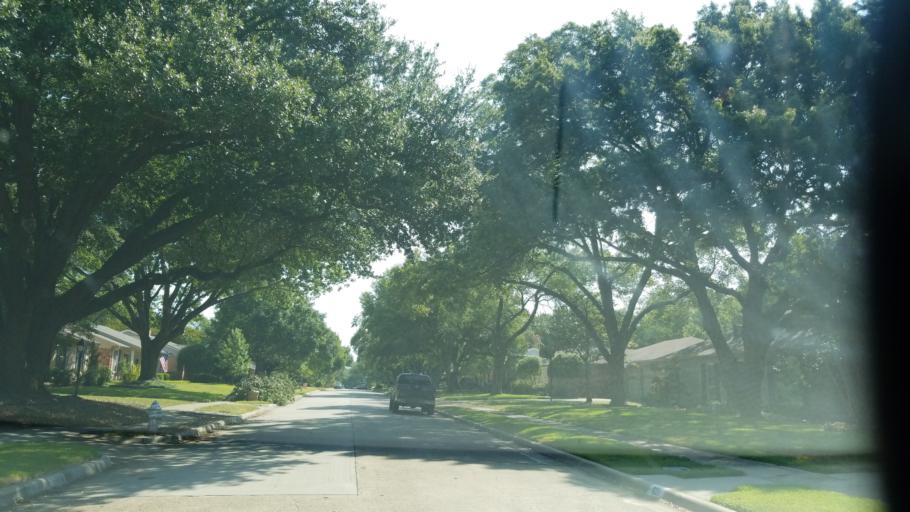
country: US
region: Texas
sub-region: Dallas County
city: Richardson
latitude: 32.9582
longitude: -96.7421
